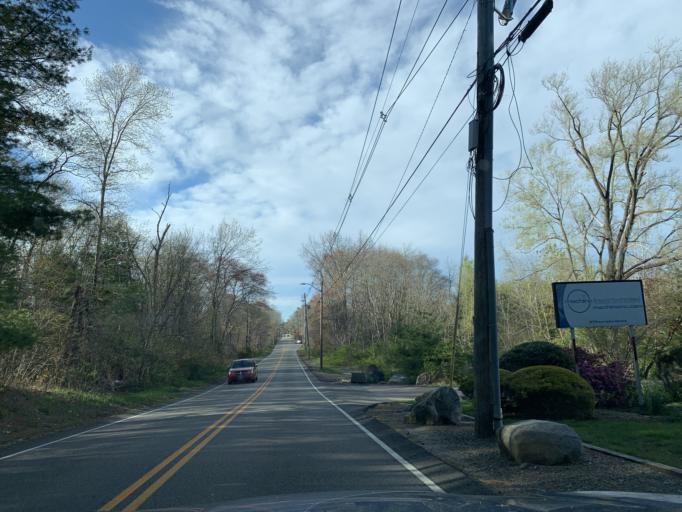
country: US
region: Massachusetts
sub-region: Norfolk County
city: Stoughton
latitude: 42.1320
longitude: -71.0756
